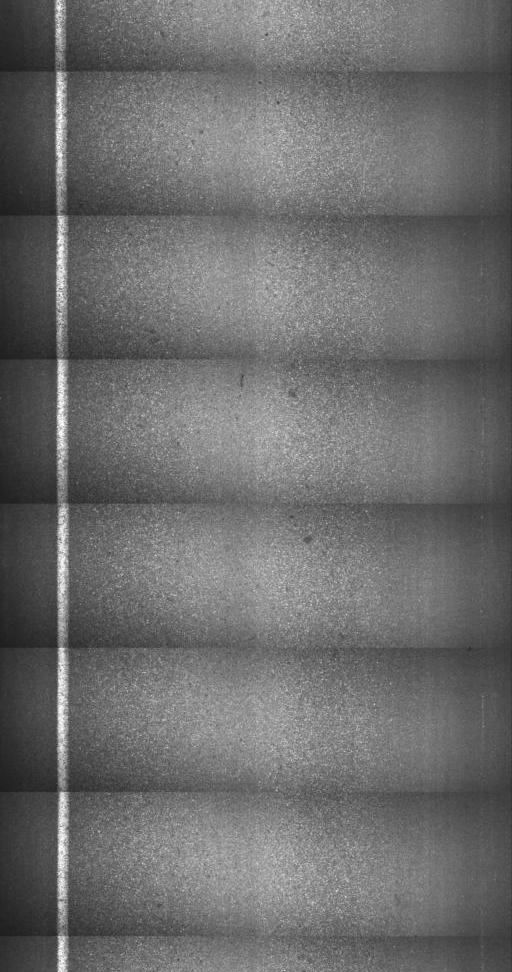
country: US
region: Vermont
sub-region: Chittenden County
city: Jericho
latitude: 44.3789
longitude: -72.9103
